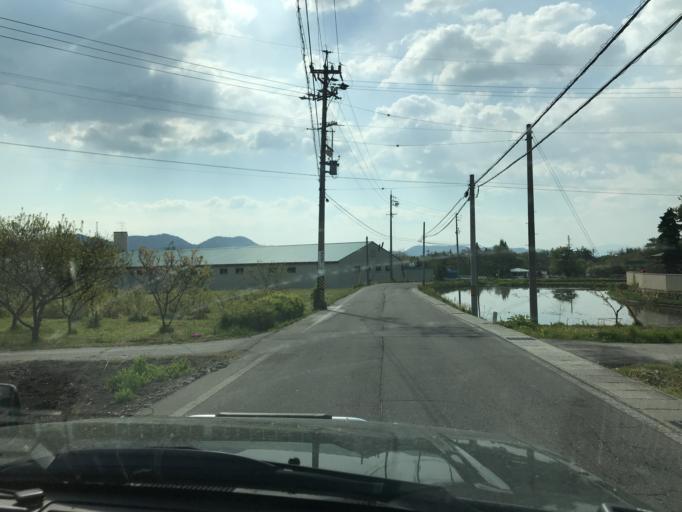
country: JP
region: Nagano
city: Omachi
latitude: 36.5143
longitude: 137.8147
